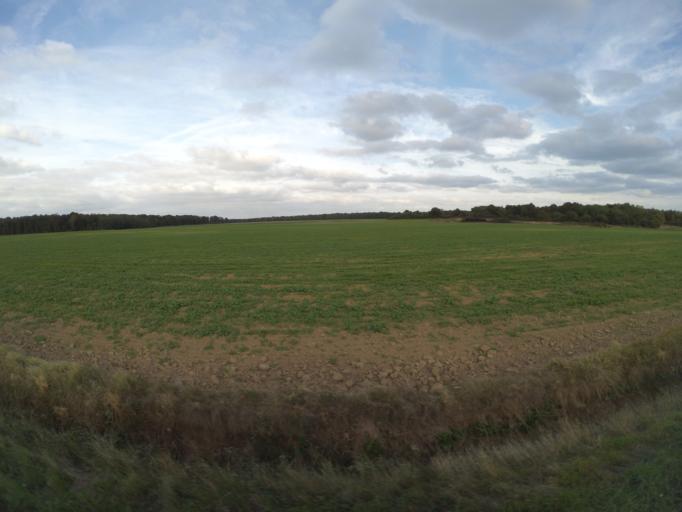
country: FR
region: Centre
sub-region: Departement d'Indre-et-Loire
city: Nazelles-Negron
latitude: 47.4588
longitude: 0.9299
